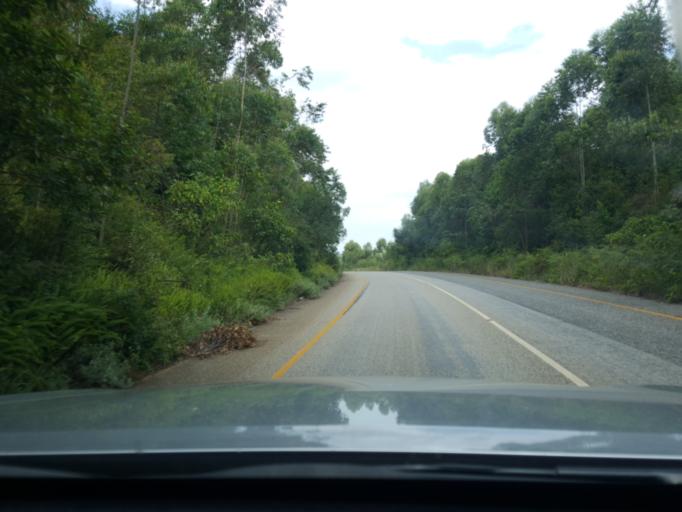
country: ZA
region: Mpumalanga
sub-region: Ehlanzeni District
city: White River
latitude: -25.1819
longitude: 30.8831
